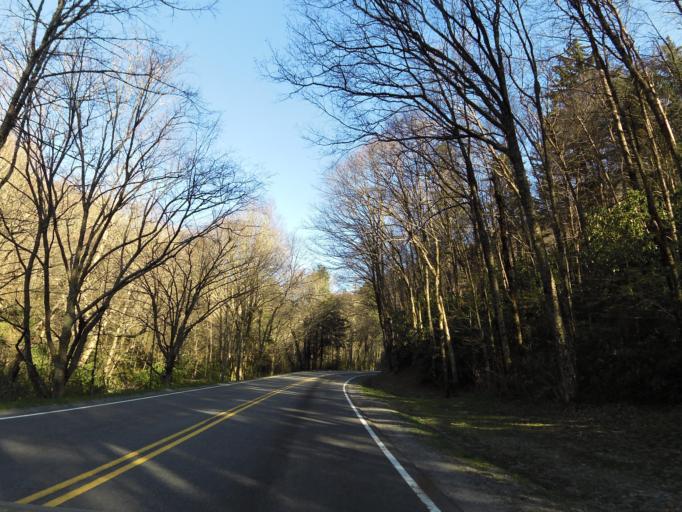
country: US
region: Tennessee
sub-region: Sevier County
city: Gatlinburg
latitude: 35.6238
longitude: -83.4443
